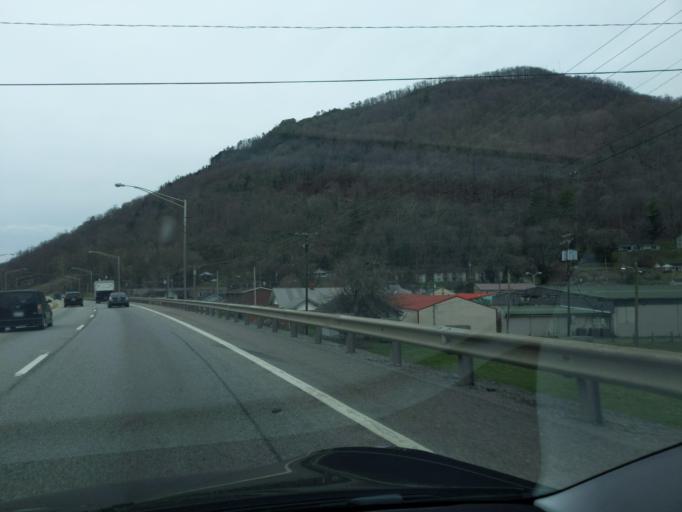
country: US
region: Kentucky
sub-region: Bell County
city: Pineville
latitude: 36.7605
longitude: -83.6935
